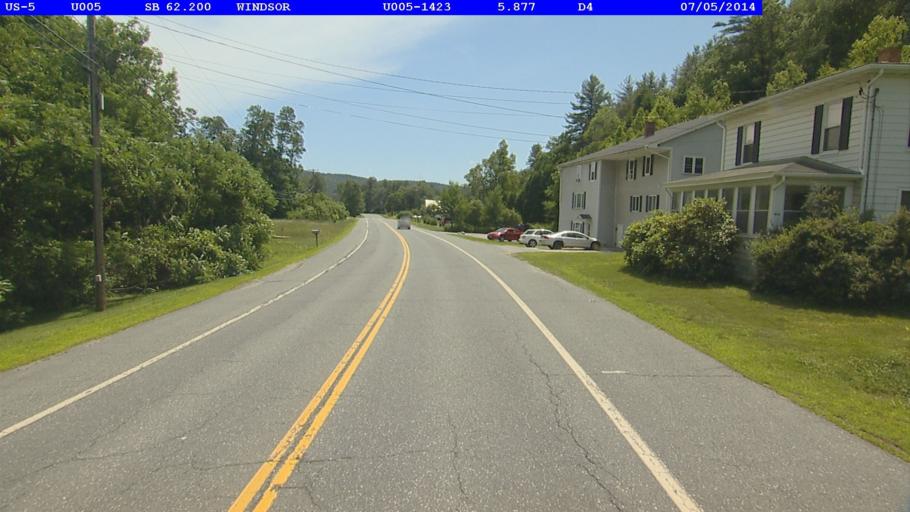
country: US
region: Vermont
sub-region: Windsor County
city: Windsor
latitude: 43.5069
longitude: -72.4019
